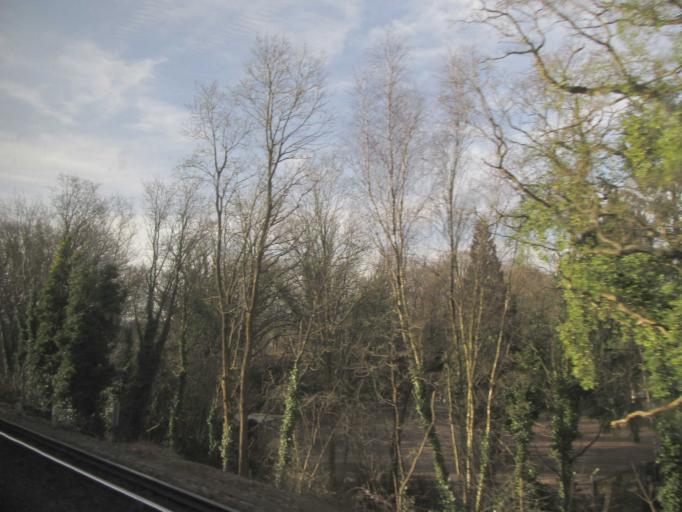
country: GB
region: England
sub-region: Surrey
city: Seale
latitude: 51.2565
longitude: -0.7225
